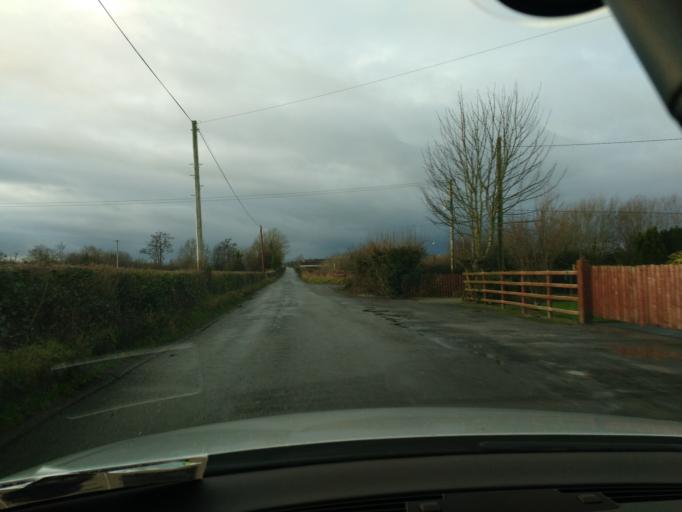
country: IE
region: Munster
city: Thurles
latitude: 52.6355
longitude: -7.8330
